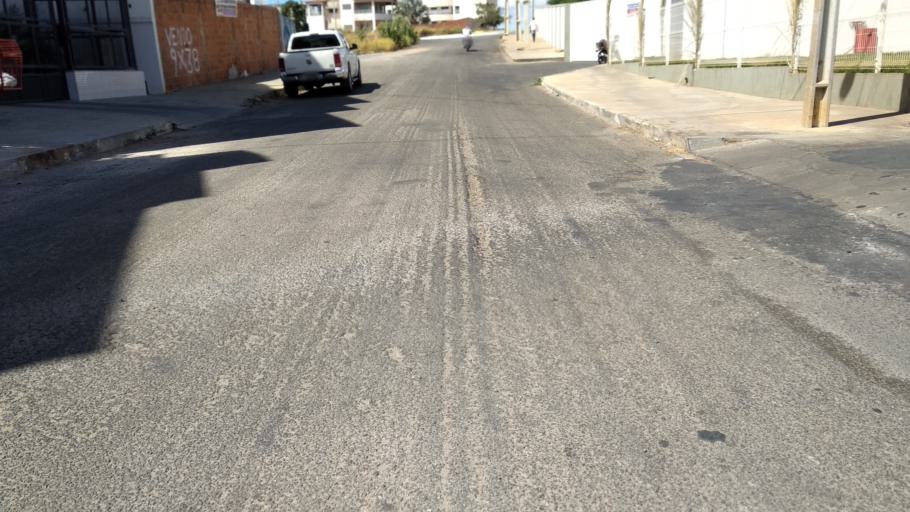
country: BR
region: Bahia
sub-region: Guanambi
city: Guanambi
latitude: -14.2268
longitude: -42.7763
